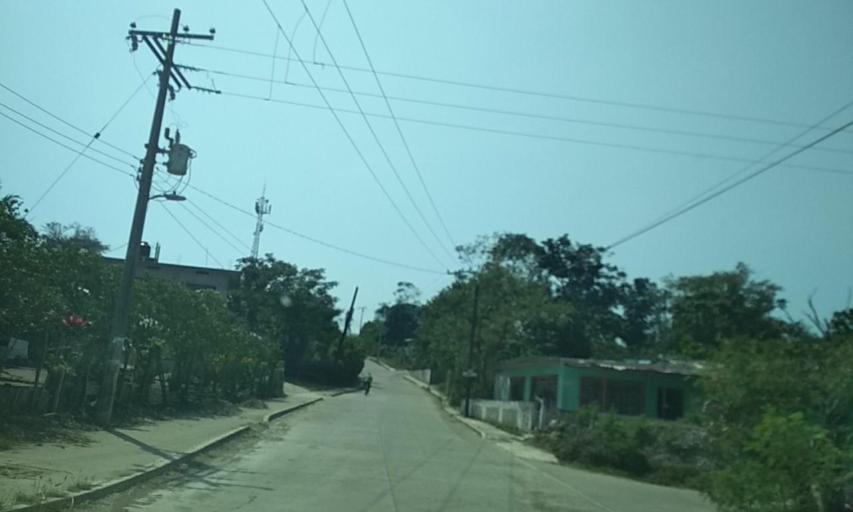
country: MX
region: Veracruz
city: Gutierrez Zamora
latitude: 20.4213
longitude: -97.1865
